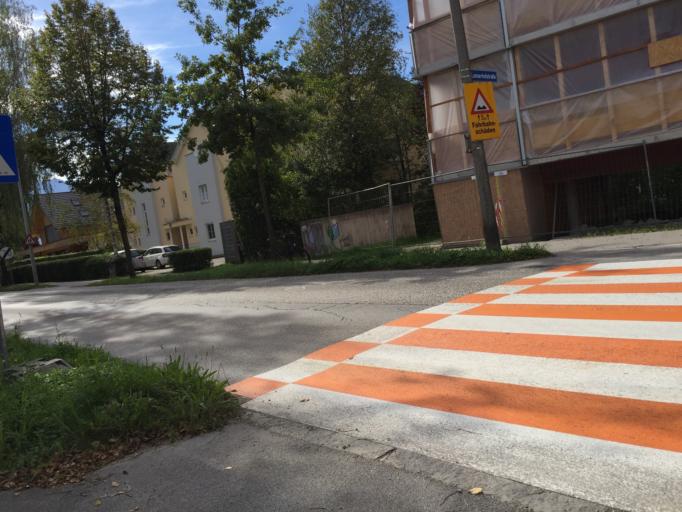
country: AT
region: Salzburg
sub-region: Salzburg Stadt
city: Salzburg
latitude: 47.7896
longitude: 13.0279
